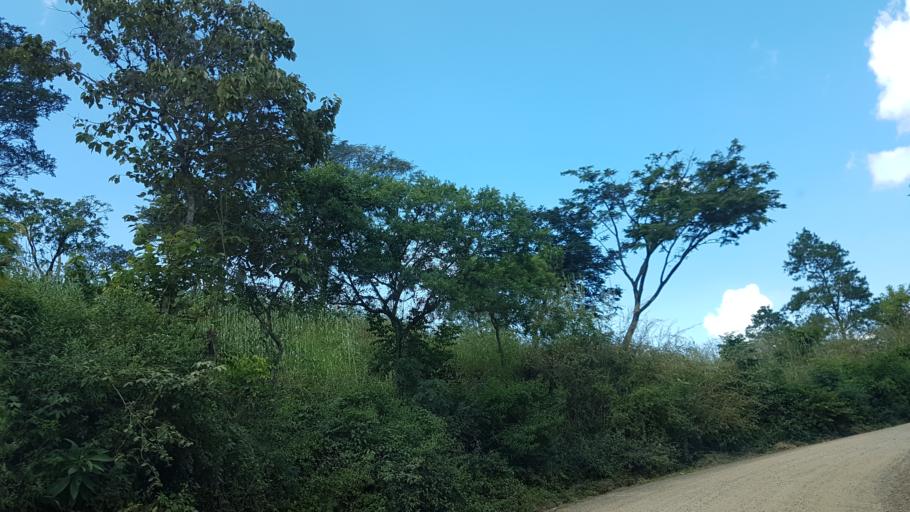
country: HN
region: El Paraiso
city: Oropoli
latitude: 13.7414
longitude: -86.7037
